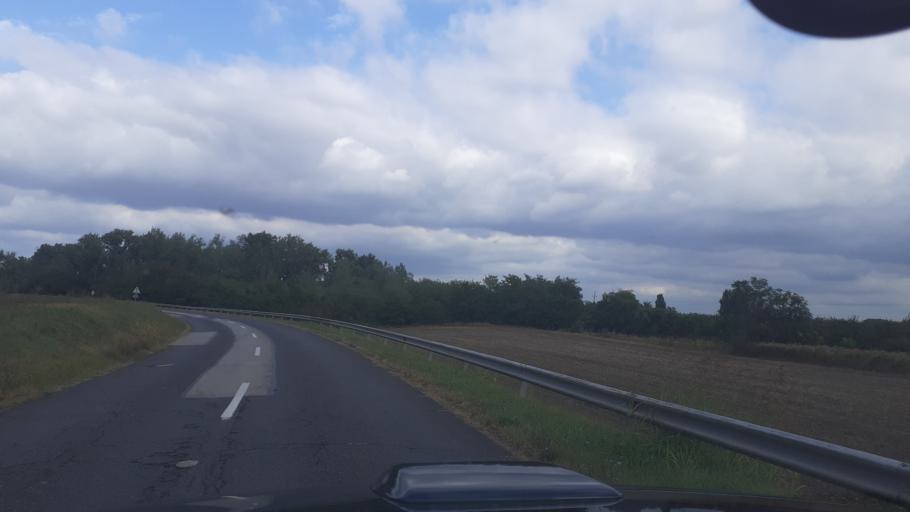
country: HU
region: Bacs-Kiskun
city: Dunavecse
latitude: 46.9292
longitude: 18.9807
